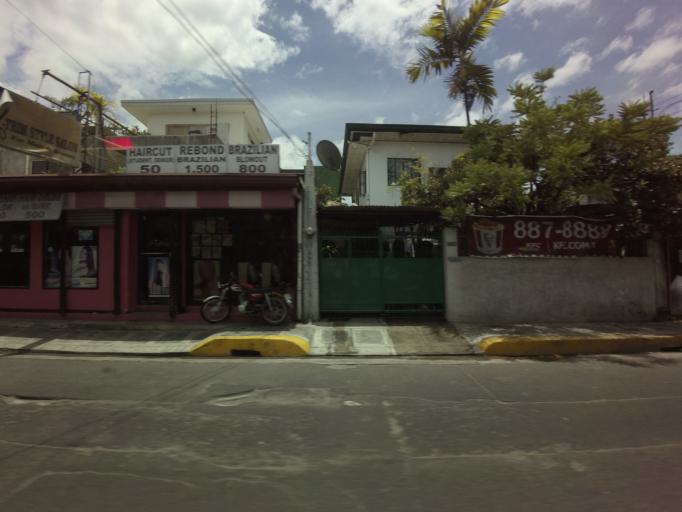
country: PH
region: Metro Manila
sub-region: Marikina
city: Calumpang
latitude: 14.6032
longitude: 121.0999
